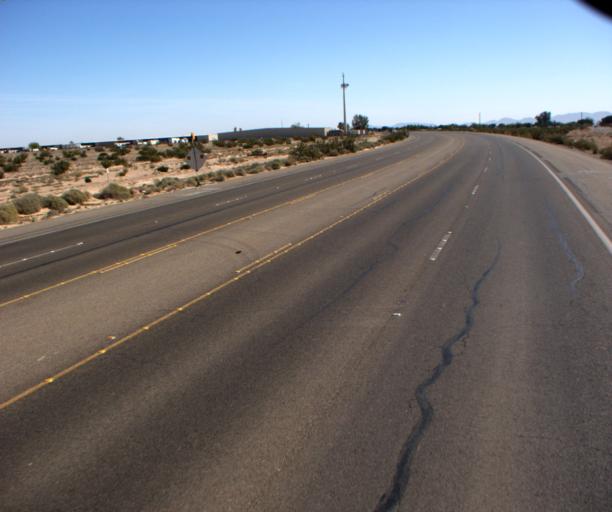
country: US
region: Arizona
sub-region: Yuma County
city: Somerton
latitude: 32.5966
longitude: -114.6713
